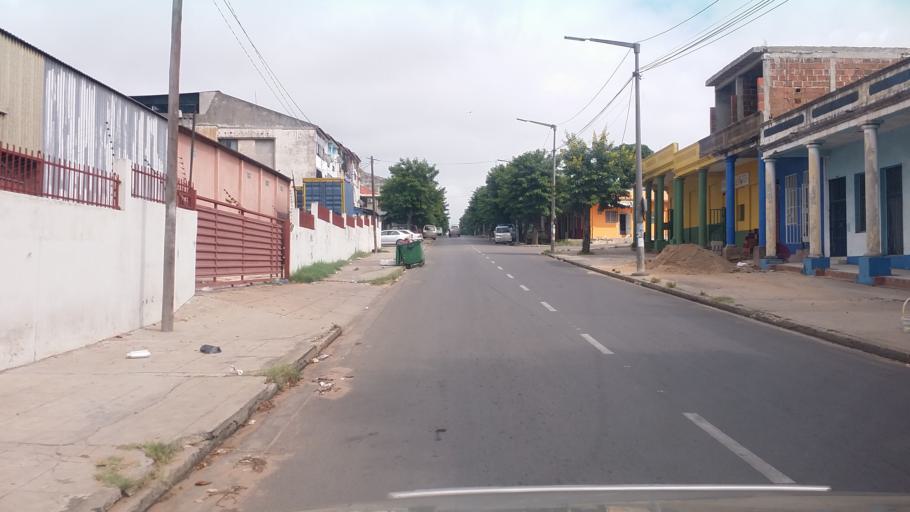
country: MZ
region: Maputo City
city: Maputo
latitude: -25.9621
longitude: 32.5619
